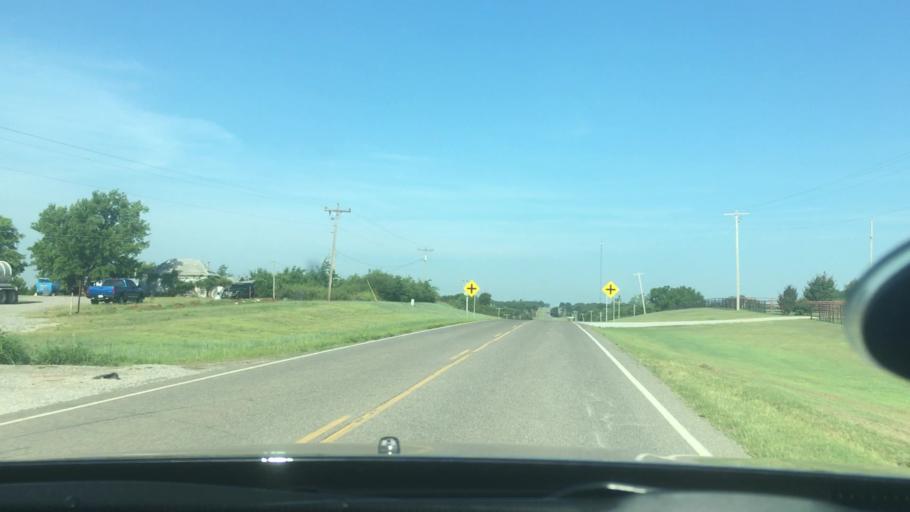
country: US
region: Oklahoma
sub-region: Garvin County
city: Wynnewood
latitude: 34.6518
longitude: -97.2439
